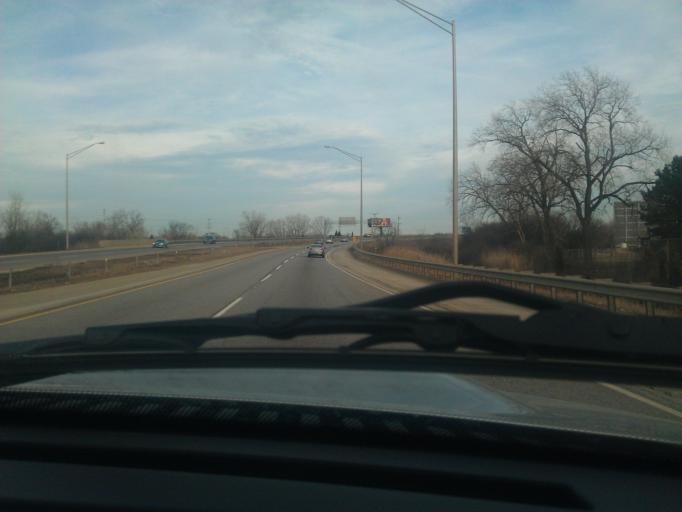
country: US
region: Illinois
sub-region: Lake County
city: Deerfield
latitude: 42.1495
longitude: -87.8452
